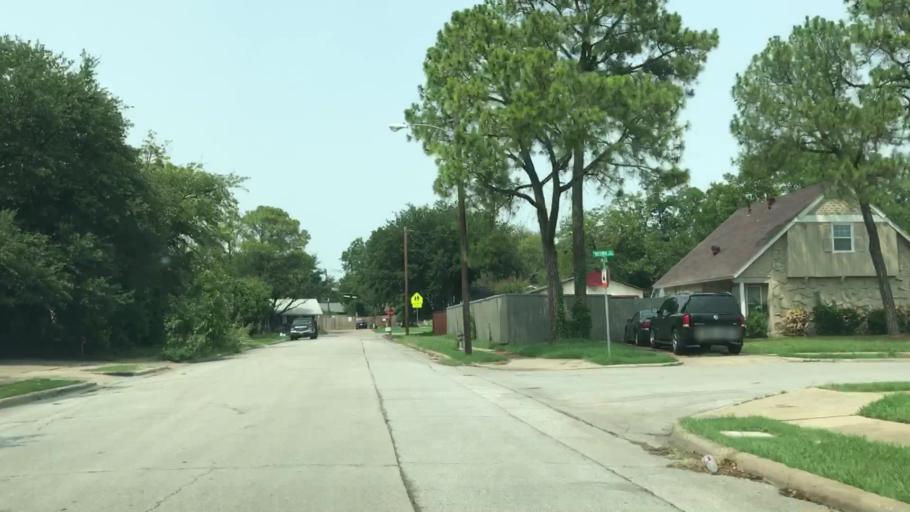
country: US
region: Texas
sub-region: Dallas County
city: Irving
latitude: 32.8502
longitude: -96.9648
